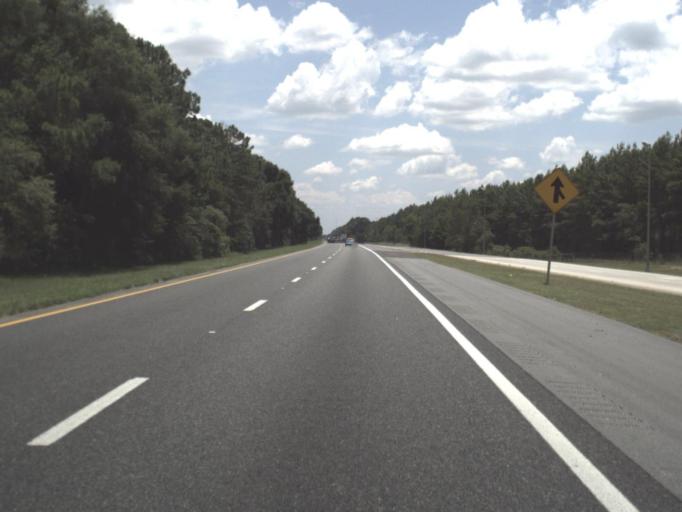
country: US
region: Florida
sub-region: Madison County
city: Madison
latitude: 30.3724
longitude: -83.2664
